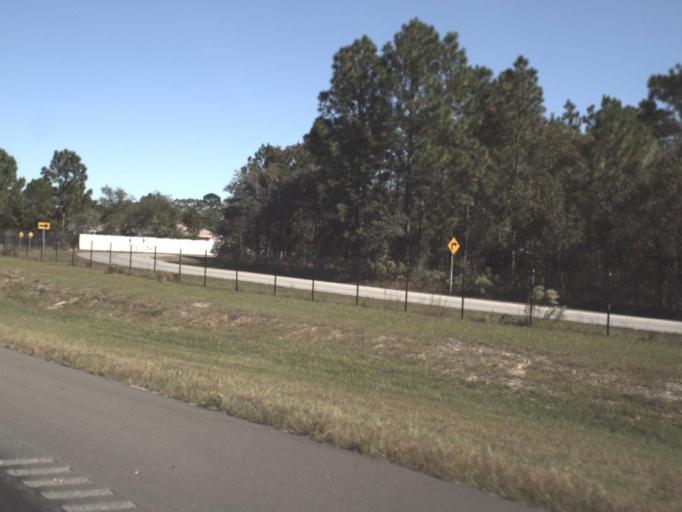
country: US
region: Florida
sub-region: Hernando County
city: Brookridge
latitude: 28.5011
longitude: -82.4767
